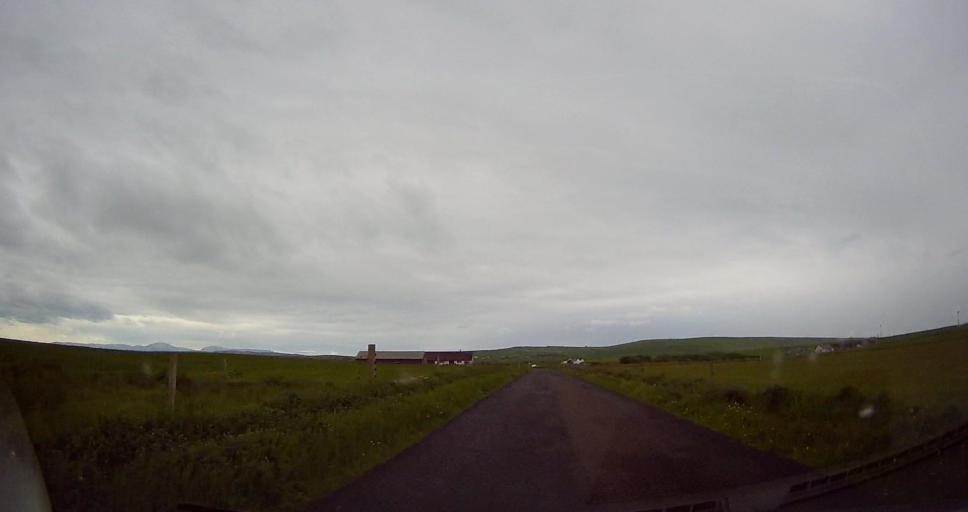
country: GB
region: Scotland
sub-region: Orkney Islands
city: Stromness
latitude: 59.0993
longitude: -3.2660
